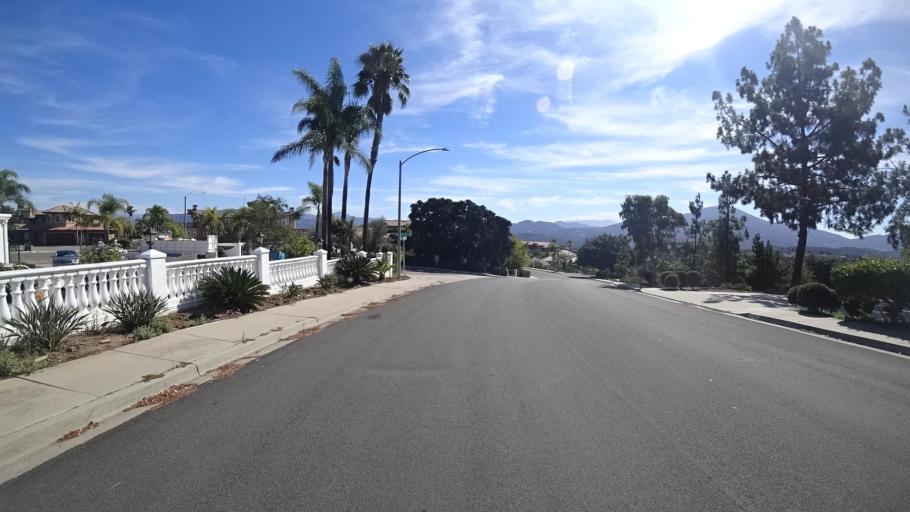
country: US
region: California
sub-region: San Diego County
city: Casa de Oro-Mount Helix
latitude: 32.7567
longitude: -116.9530
